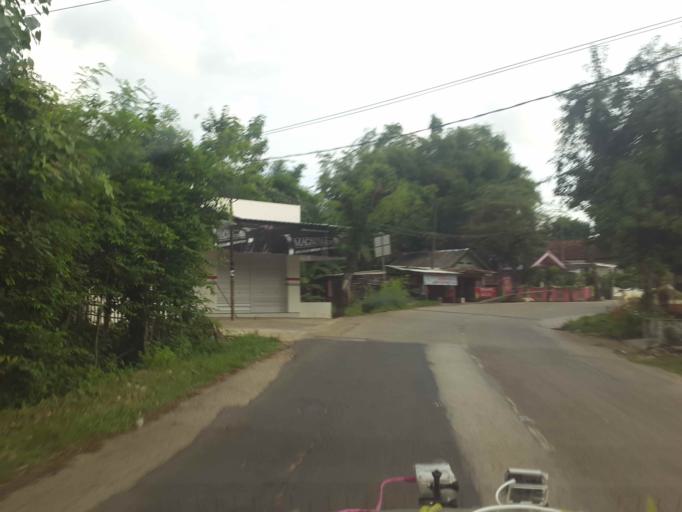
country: ID
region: East Java
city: Senmasen
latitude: -6.9953
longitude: 113.8669
